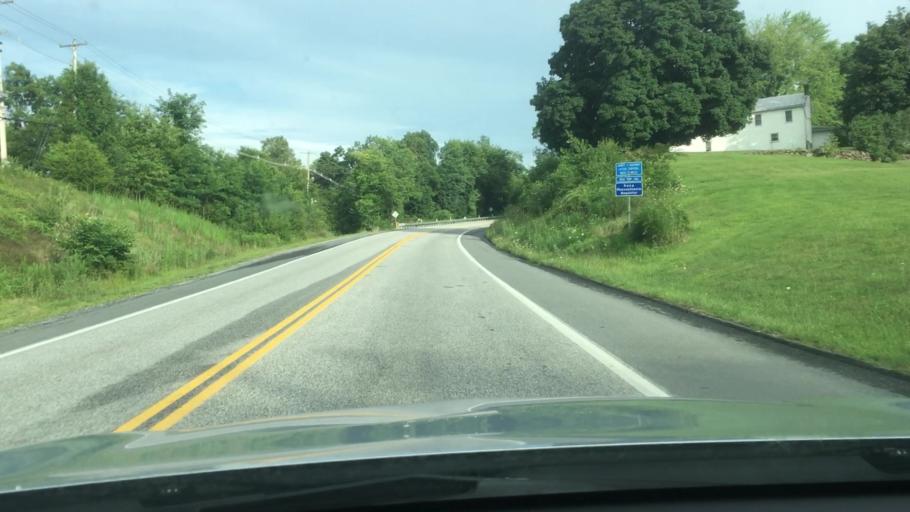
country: US
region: Pennsylvania
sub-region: York County
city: Dover
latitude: 40.0777
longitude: -76.9280
